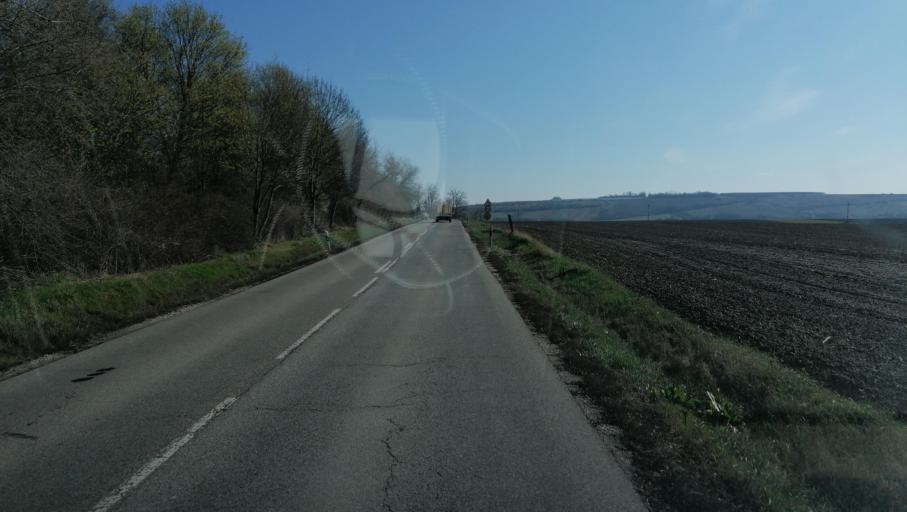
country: HU
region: Pest
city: Perbal
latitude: 47.6055
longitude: 18.7708
